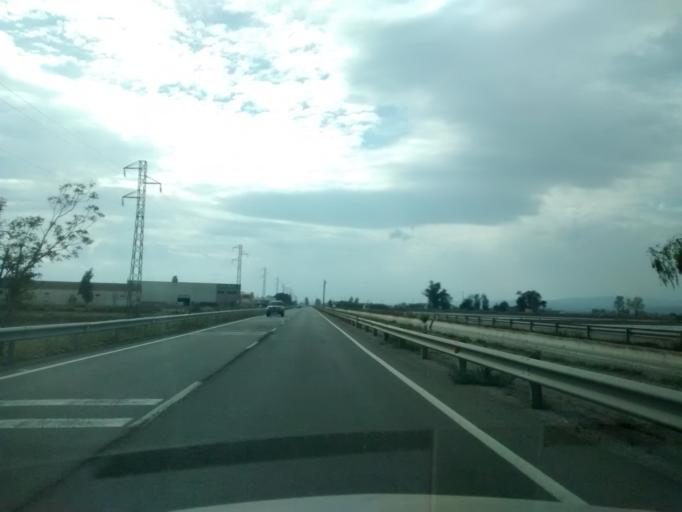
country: ES
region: Catalonia
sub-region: Provincia de Tarragona
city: Deltebre
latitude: 40.7263
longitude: 0.7099
